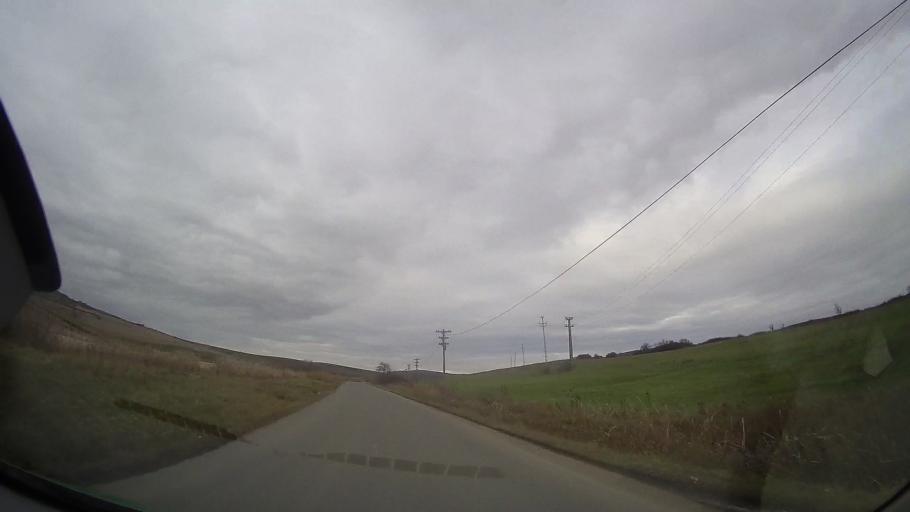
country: RO
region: Mures
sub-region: Comuna Faragau
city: Faragau
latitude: 46.7435
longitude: 24.5351
